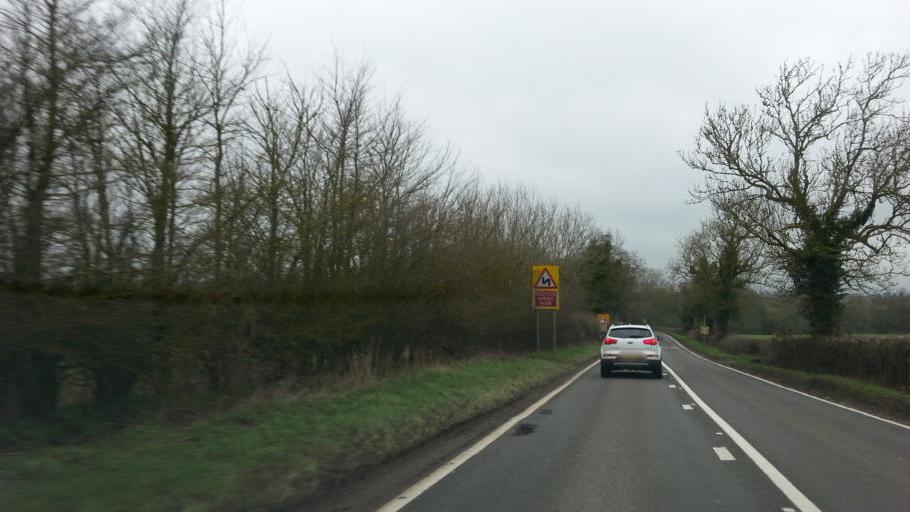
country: GB
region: England
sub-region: Northamptonshire
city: Brackley
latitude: 52.0571
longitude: -1.2328
